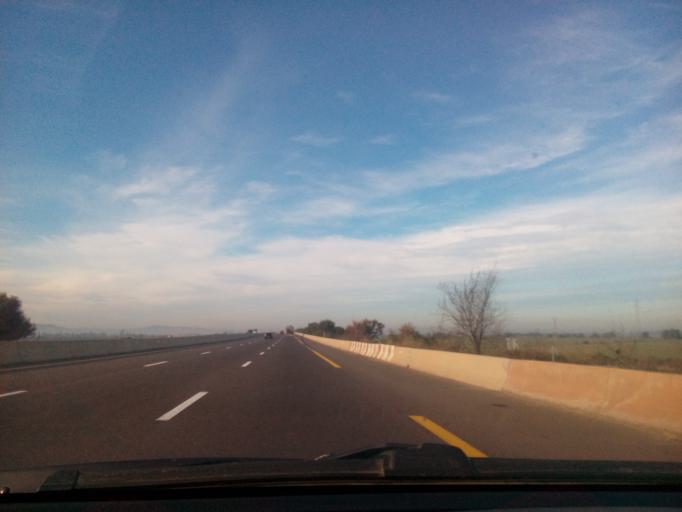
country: DZ
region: Mascara
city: Sig
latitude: 35.6140
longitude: -0.0103
